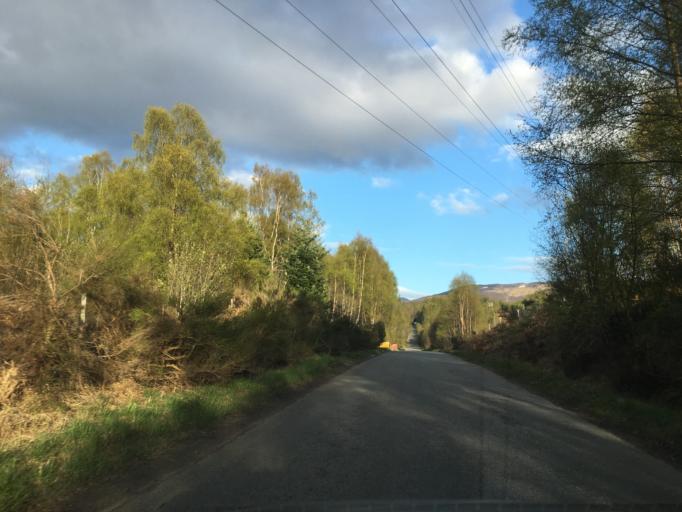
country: GB
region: Scotland
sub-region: Perth and Kinross
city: Aberfeldy
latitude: 56.7057
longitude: -4.0085
